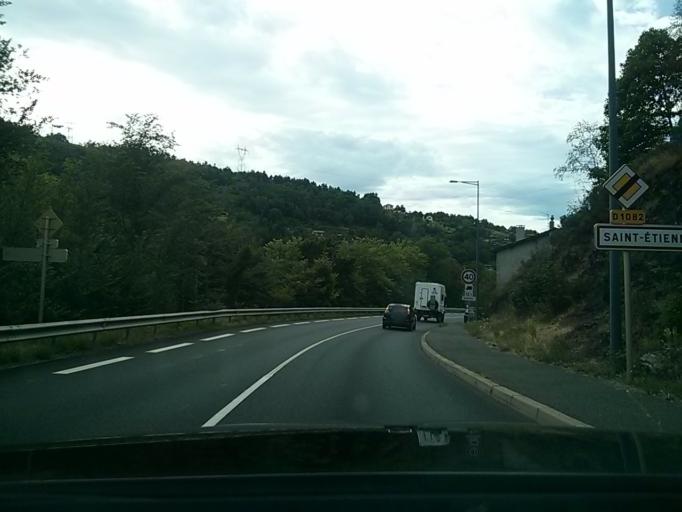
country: FR
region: Rhone-Alpes
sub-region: Departement de la Loire
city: Saint-Etienne
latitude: 45.4027
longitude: 4.4032
